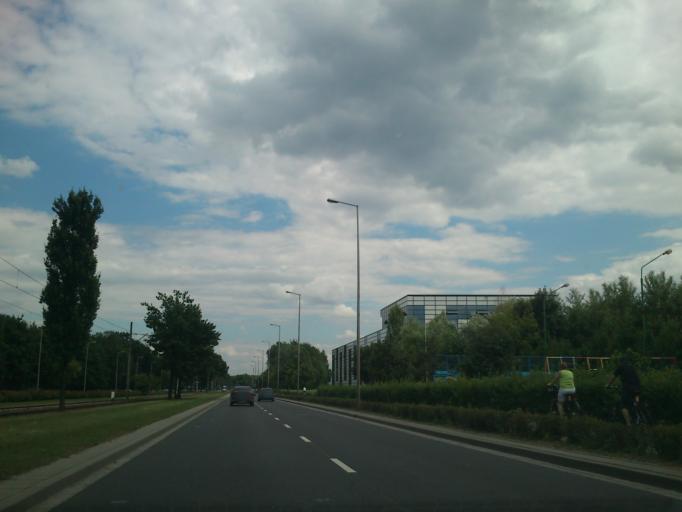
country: PL
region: Lower Silesian Voivodeship
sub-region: Powiat wroclawski
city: Wroclaw
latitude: 51.1321
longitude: 16.9601
